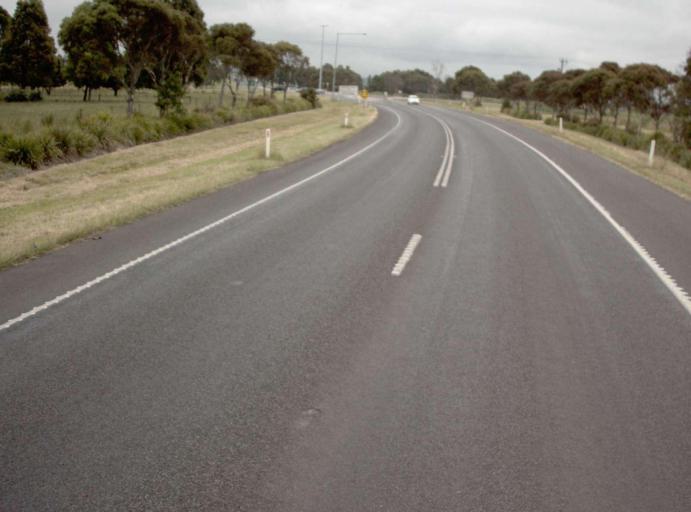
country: AU
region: Victoria
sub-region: Latrobe
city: Morwell
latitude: -38.2496
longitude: 146.4267
